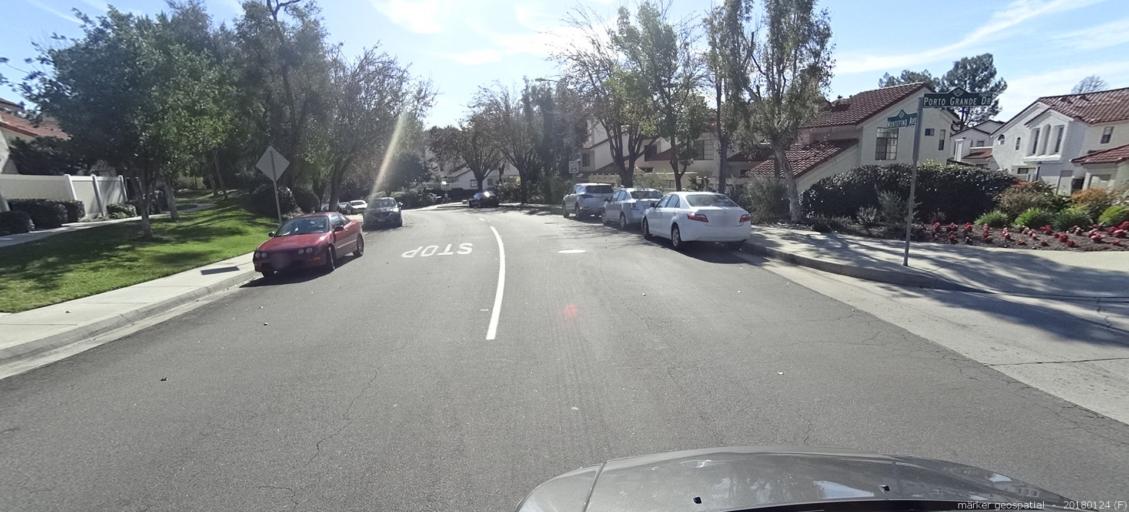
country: US
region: California
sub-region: Los Angeles County
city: Diamond Bar
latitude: 33.9993
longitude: -117.8155
